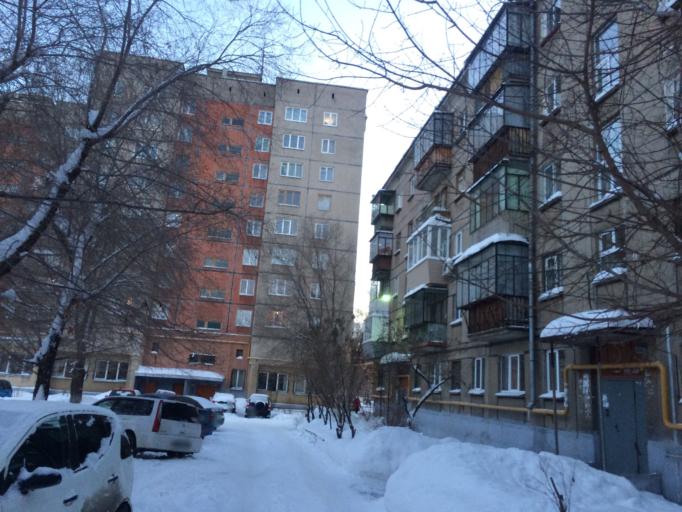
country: RU
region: Chelyabinsk
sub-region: Gorod Magnitogorsk
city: Magnitogorsk
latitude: 53.4057
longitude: 58.9722
